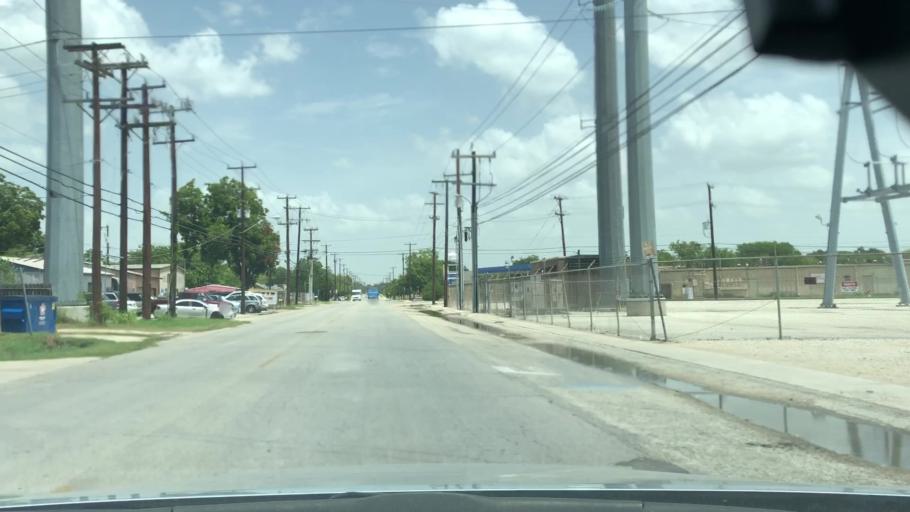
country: US
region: Texas
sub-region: Bexar County
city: Kirby
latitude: 29.4657
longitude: -98.3929
